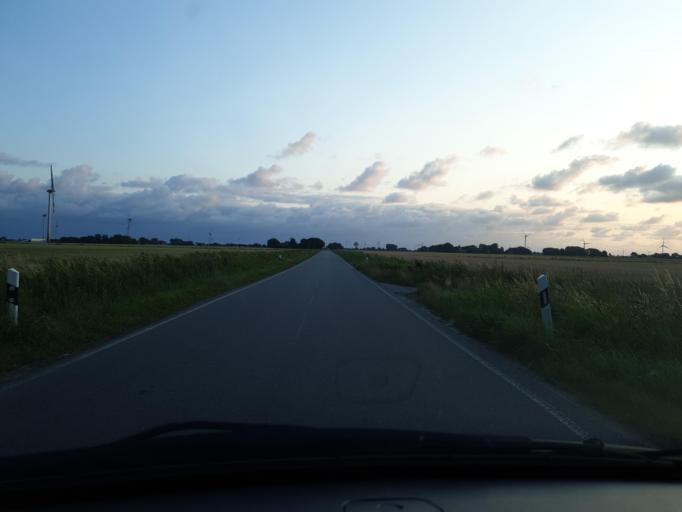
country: DE
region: Schleswig-Holstein
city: Diekhusen-Fahrstedt
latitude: 53.9402
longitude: 9.0118
